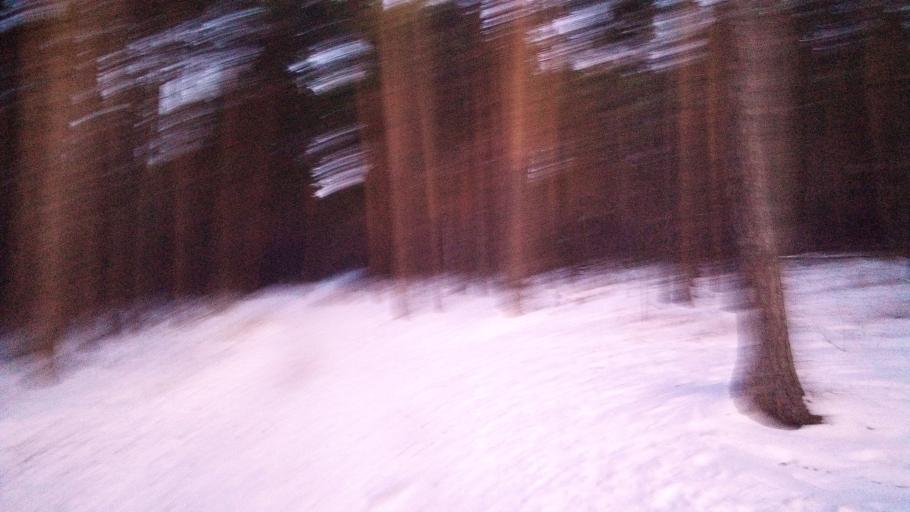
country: RU
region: Chelyabinsk
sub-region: Gorod Chelyabinsk
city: Chelyabinsk
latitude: 55.1656
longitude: 61.3317
